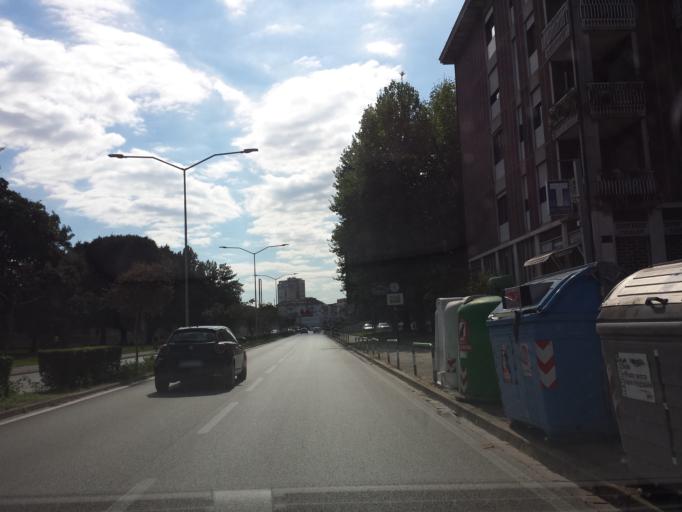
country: IT
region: Veneto
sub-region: Provincia di Vicenza
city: Vicenza
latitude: 45.5512
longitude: 11.5351
